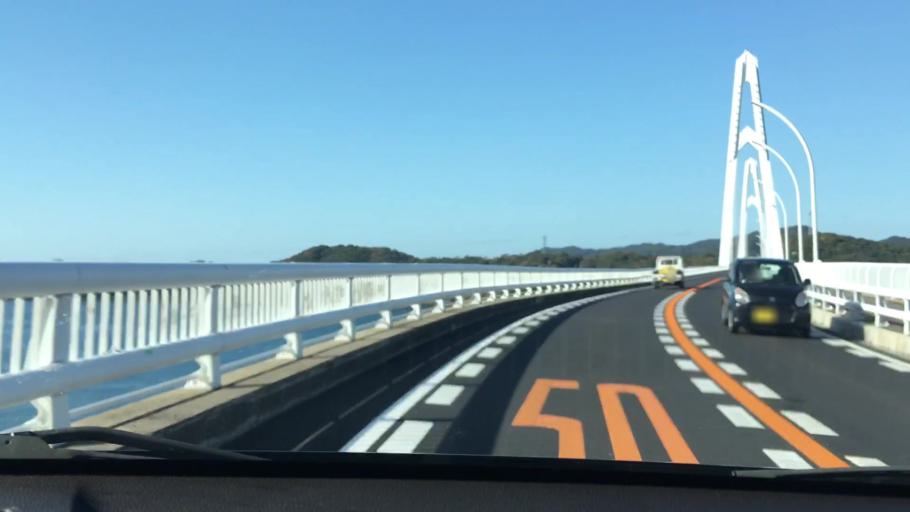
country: JP
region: Nagasaki
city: Sasebo
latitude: 33.0366
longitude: 129.6475
